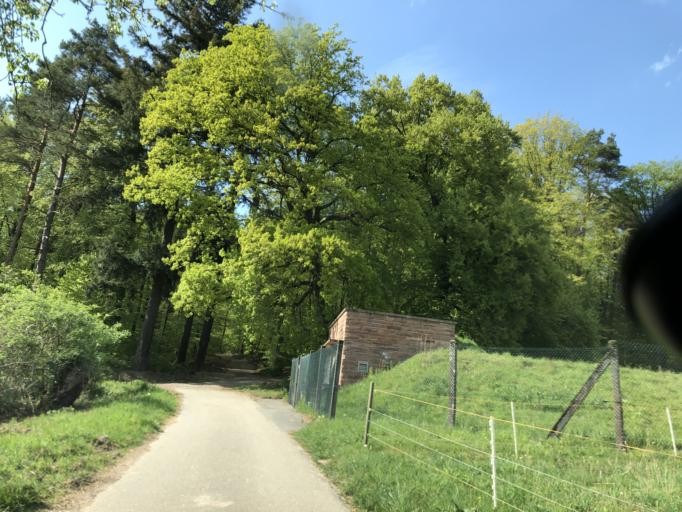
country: DE
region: Baden-Wuerttemberg
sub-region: Karlsruhe Region
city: Schonau
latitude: 49.4391
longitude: 8.8015
